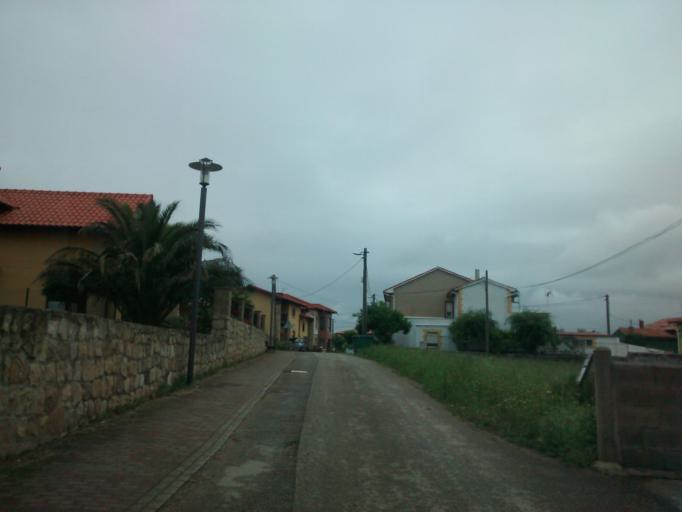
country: ES
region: Cantabria
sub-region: Provincia de Cantabria
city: Santillana
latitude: 43.4190
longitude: -4.1016
